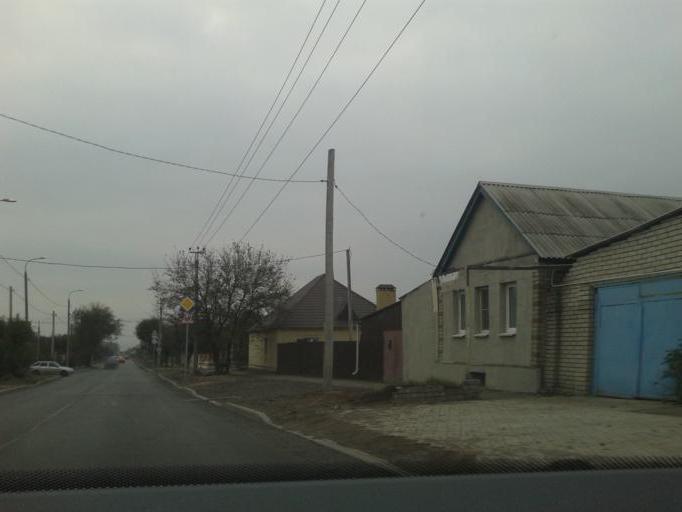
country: RU
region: Volgograd
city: Volgograd
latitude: 48.7008
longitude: 44.4641
